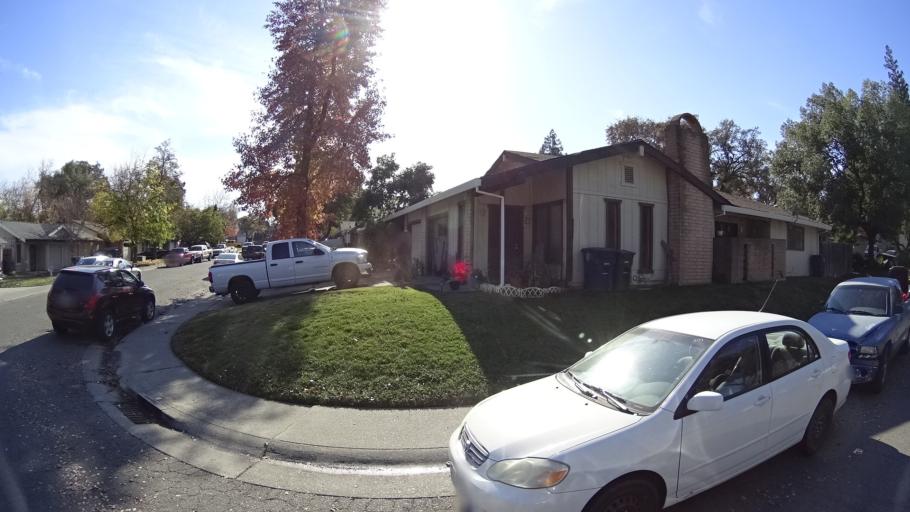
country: US
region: California
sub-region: Sacramento County
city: Fair Oaks
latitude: 38.6676
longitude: -121.2911
